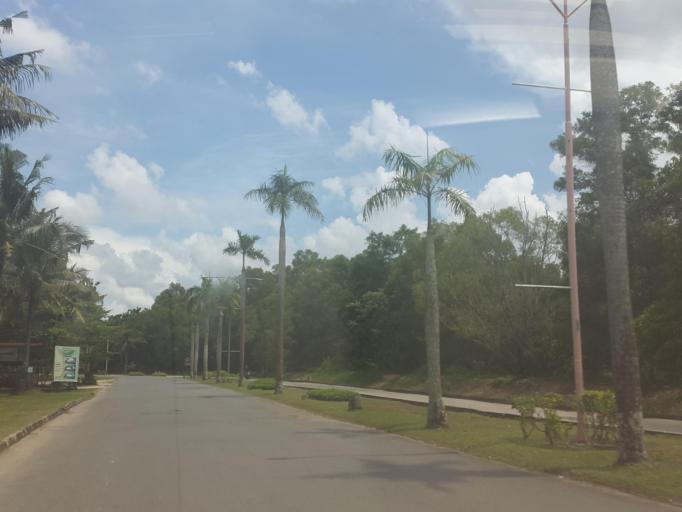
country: SG
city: Singapore
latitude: 1.0853
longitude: 103.9414
